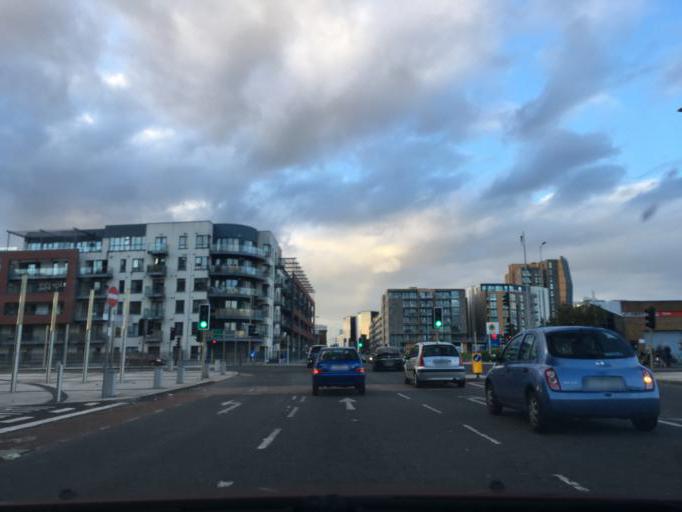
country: IE
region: Leinster
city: Tallaght
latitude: 53.2841
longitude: -6.3755
